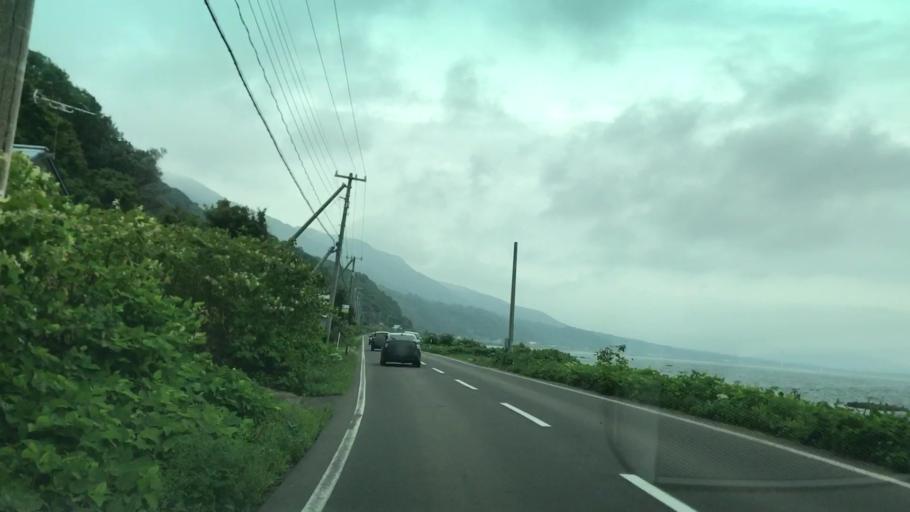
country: JP
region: Hokkaido
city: Iwanai
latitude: 42.8073
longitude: 140.3050
